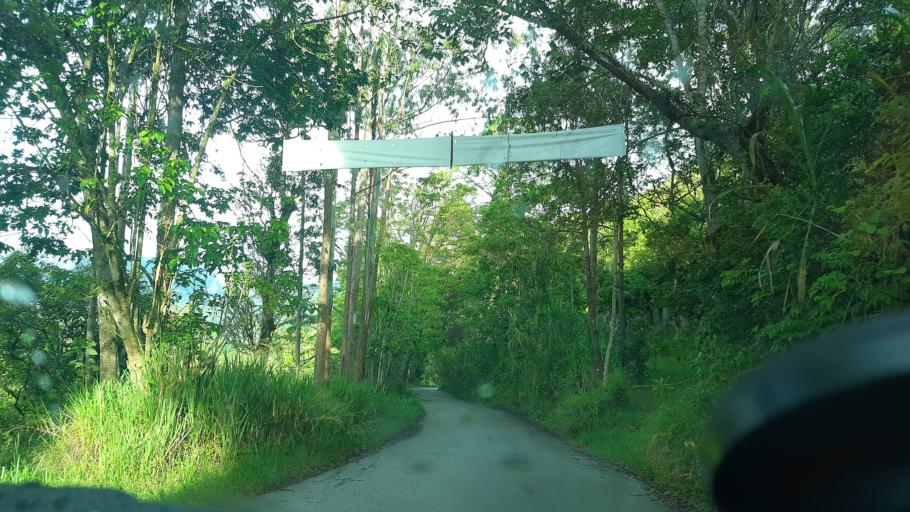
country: CO
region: Cundinamarca
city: Tenza
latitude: 5.0752
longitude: -73.4131
